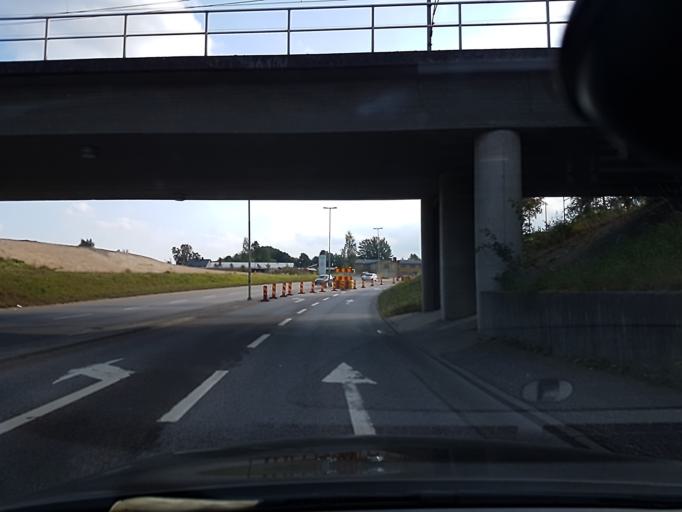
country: SE
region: Kronoberg
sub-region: Vaxjo Kommun
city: Vaexjoe
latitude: 56.8765
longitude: 14.7867
